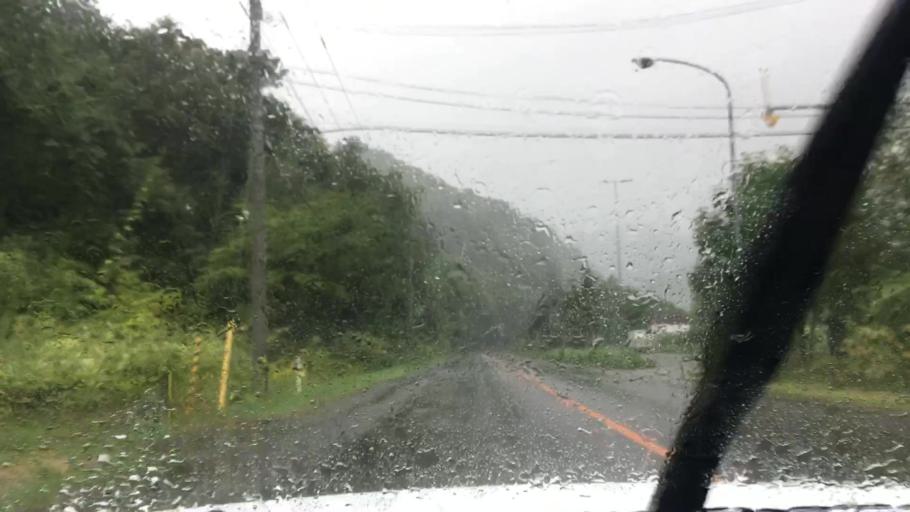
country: JP
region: Hokkaido
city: Sapporo
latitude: 42.9483
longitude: 141.1442
